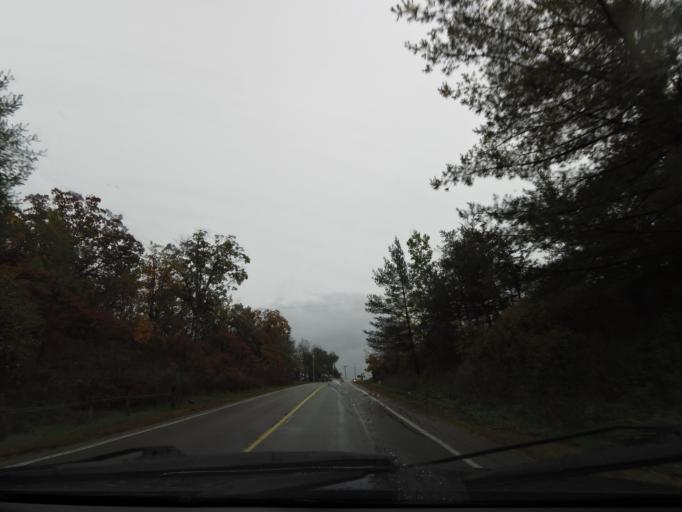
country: CA
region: Ontario
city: Burlington
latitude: 43.4335
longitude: -79.8453
